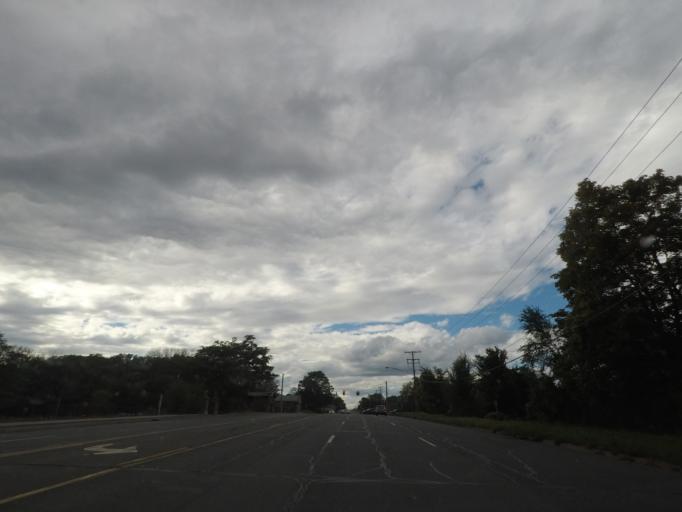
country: US
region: New York
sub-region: Albany County
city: McKownville
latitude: 42.6853
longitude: -73.8506
